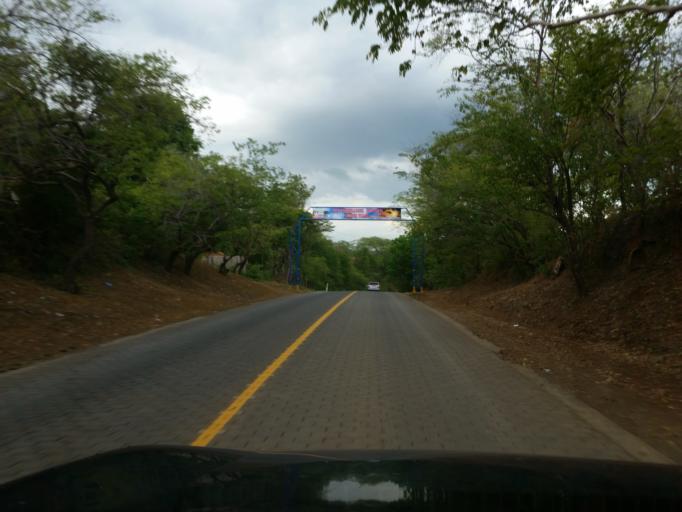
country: NI
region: Managua
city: Carlos Fonseca Amador
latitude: 11.8983
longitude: -86.5124
